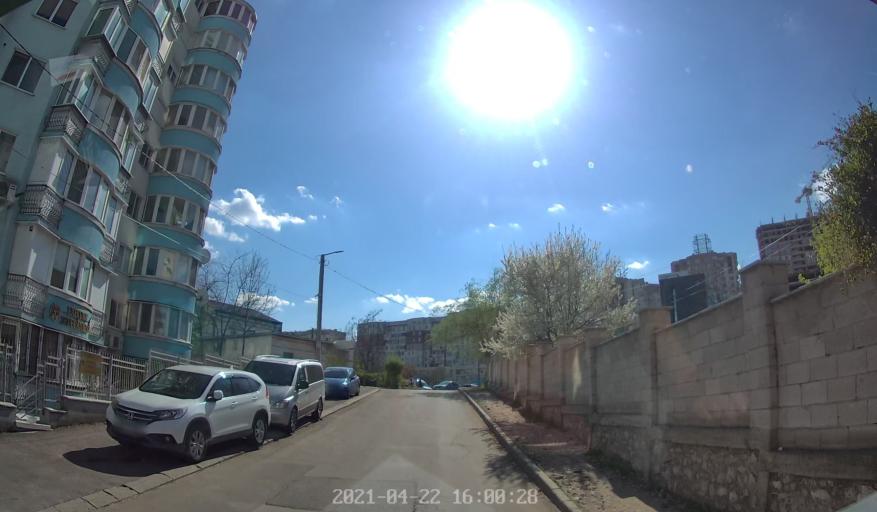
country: MD
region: Chisinau
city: Chisinau
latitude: 47.0463
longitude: 28.8935
